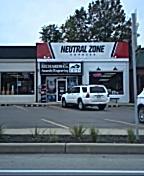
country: US
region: Kentucky
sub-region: Jefferson County
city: Middletown
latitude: 38.2456
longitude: -85.5425
